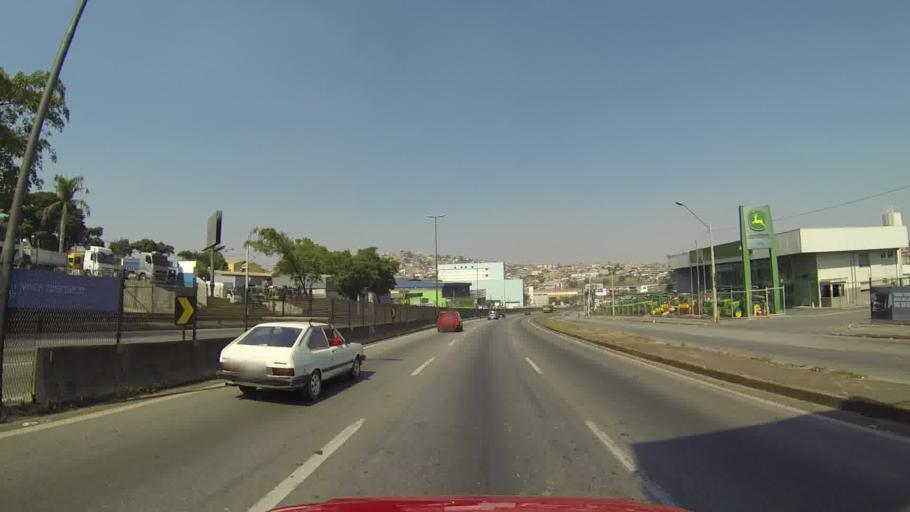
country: BR
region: Minas Gerais
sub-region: Contagem
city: Contagem
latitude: -19.9639
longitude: -44.0434
